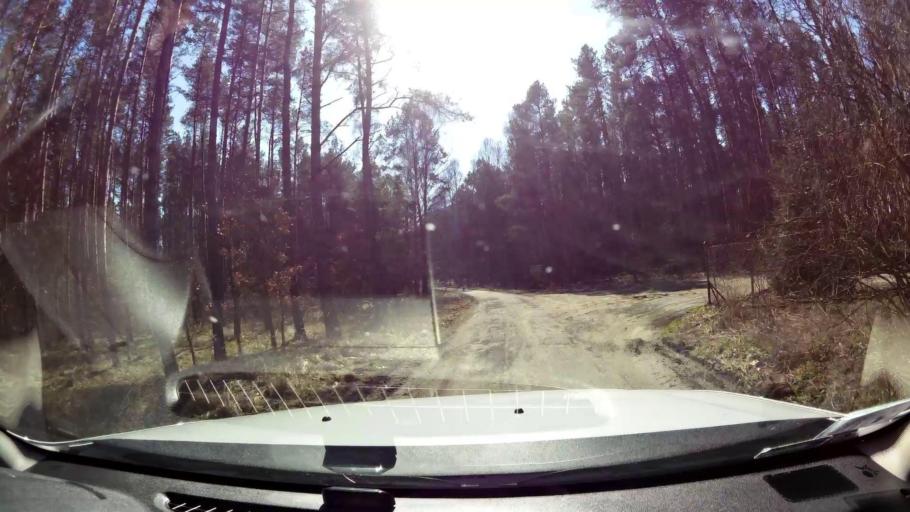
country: PL
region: West Pomeranian Voivodeship
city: Trzcinsko Zdroj
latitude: 53.0328
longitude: 14.6325
